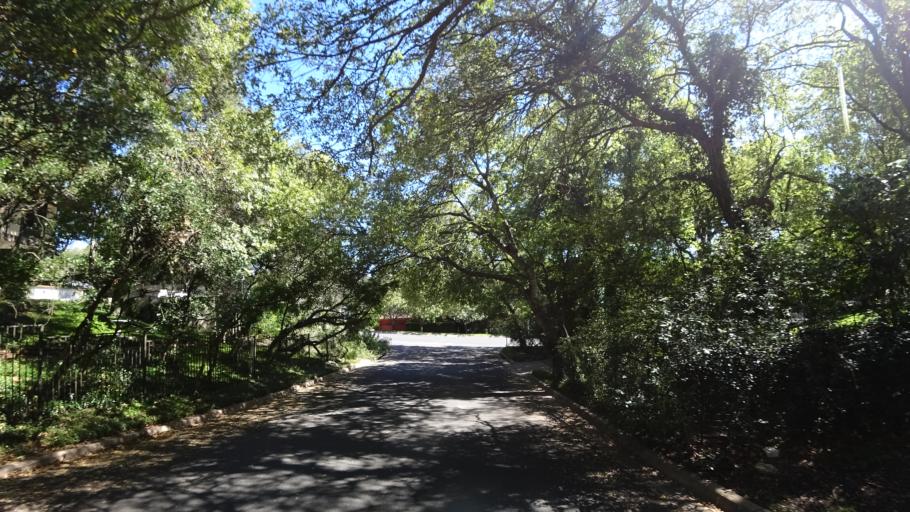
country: US
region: Texas
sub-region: Travis County
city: West Lake Hills
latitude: 30.3236
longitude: -97.7700
